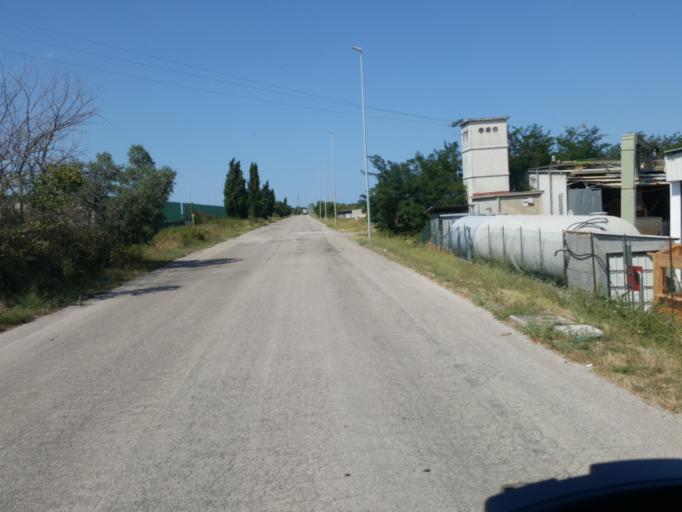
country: IT
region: Abruzzo
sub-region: Provincia di Chieti
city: Salvo Marina
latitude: 42.0612
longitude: 14.7630
